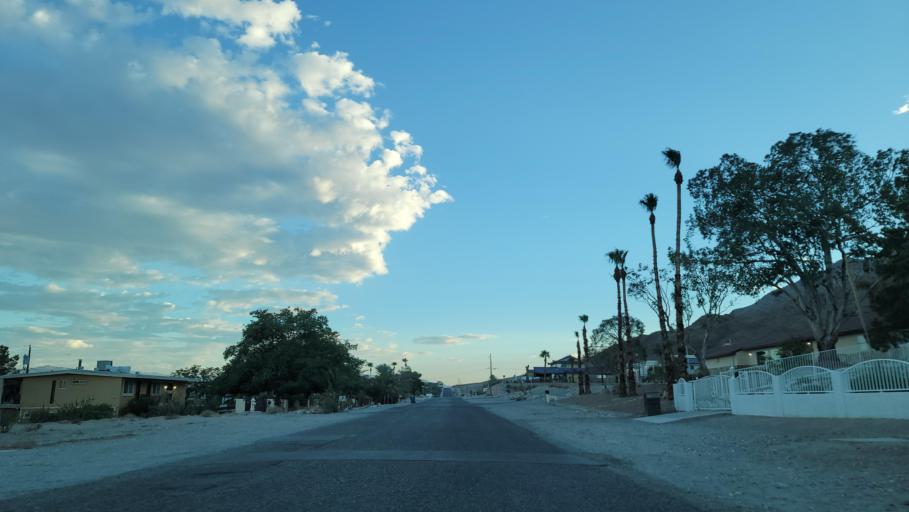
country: US
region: Nevada
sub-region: Clark County
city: Sunrise Manor
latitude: 36.1674
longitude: -115.0169
